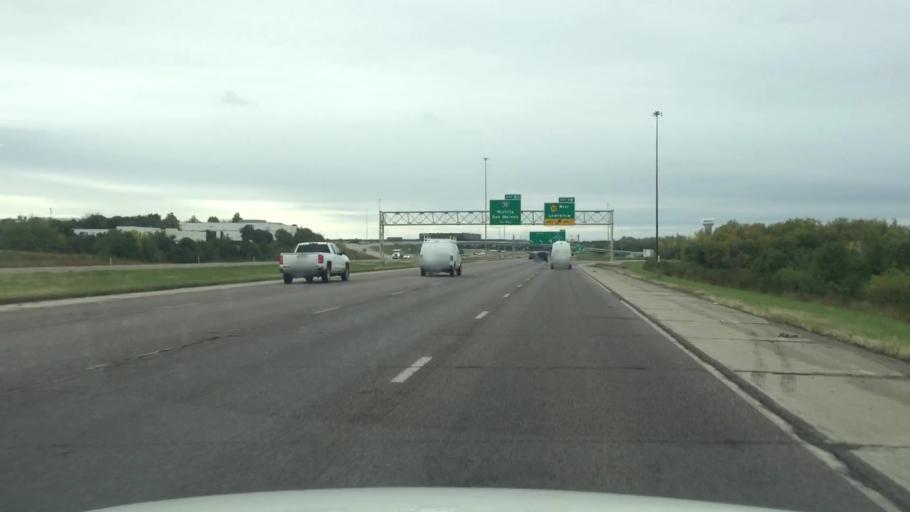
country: US
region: Kansas
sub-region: Johnson County
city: Lenexa
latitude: 38.9529
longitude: -94.7745
